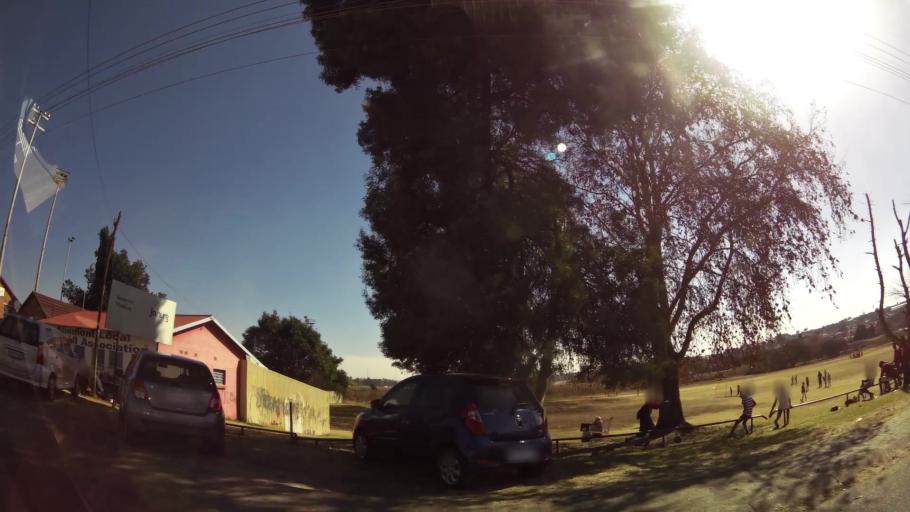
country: ZA
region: Gauteng
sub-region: City of Johannesburg Metropolitan Municipality
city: Roodepoort
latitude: -26.1950
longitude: 27.9547
